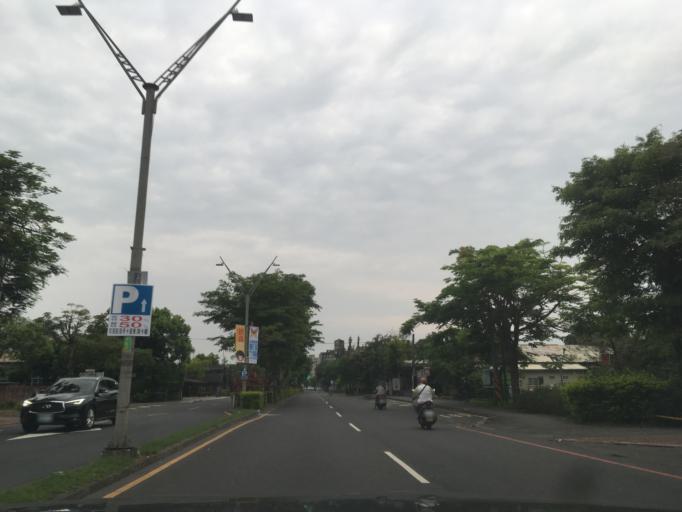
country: TW
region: Taiwan
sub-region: Yilan
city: Yilan
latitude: 24.7544
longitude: 121.7575
